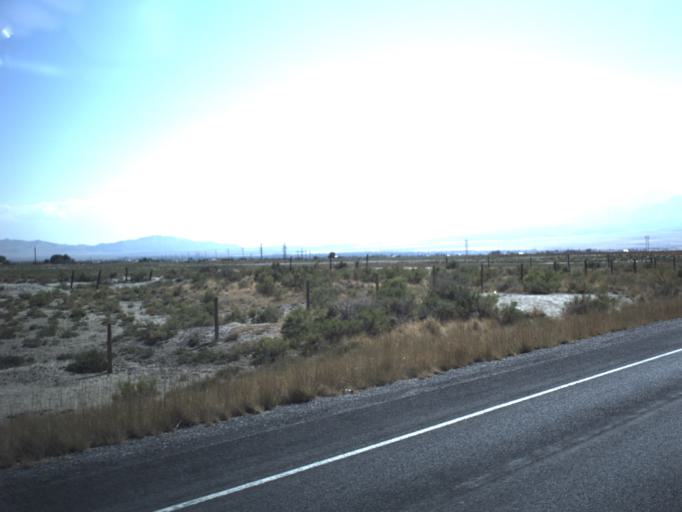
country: US
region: Utah
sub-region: Tooele County
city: Grantsville
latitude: 40.6809
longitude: -112.4424
